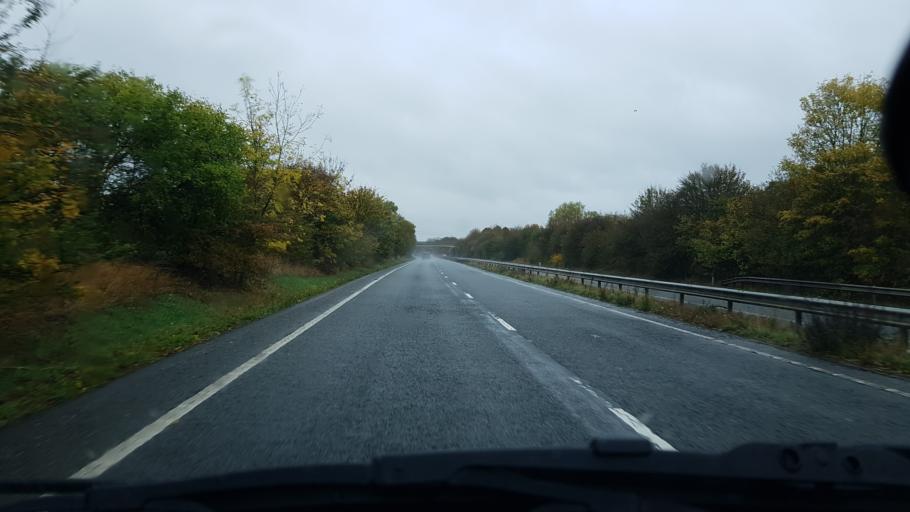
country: GB
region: England
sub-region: Oxfordshire
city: Witney
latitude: 51.7766
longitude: -1.5082
